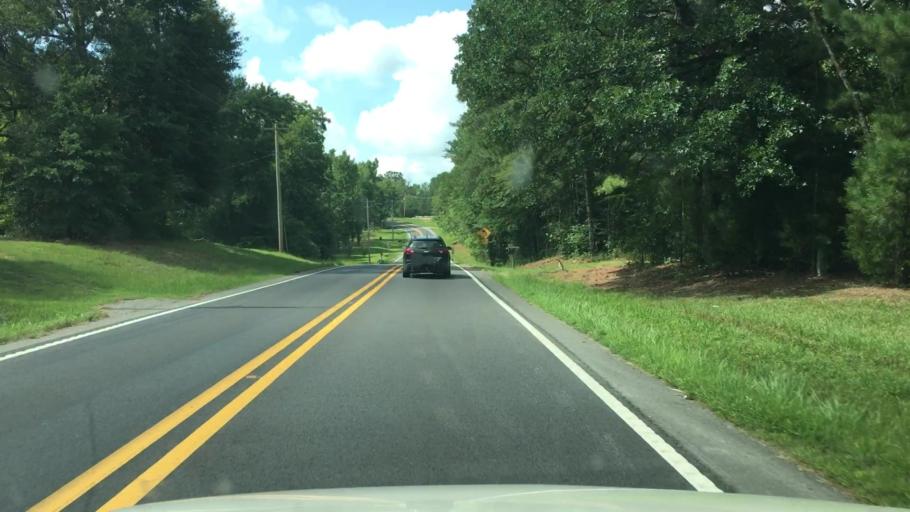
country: US
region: Arkansas
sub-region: Garland County
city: Lake Hamilton
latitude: 34.2937
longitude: -93.1626
